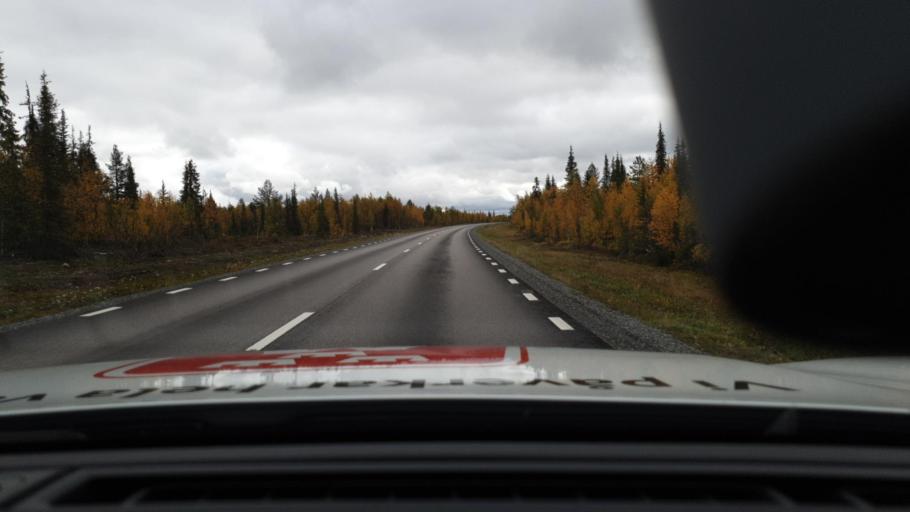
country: SE
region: Norrbotten
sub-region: Gallivare Kommun
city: Malmberget
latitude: 67.5776
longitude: 21.1374
